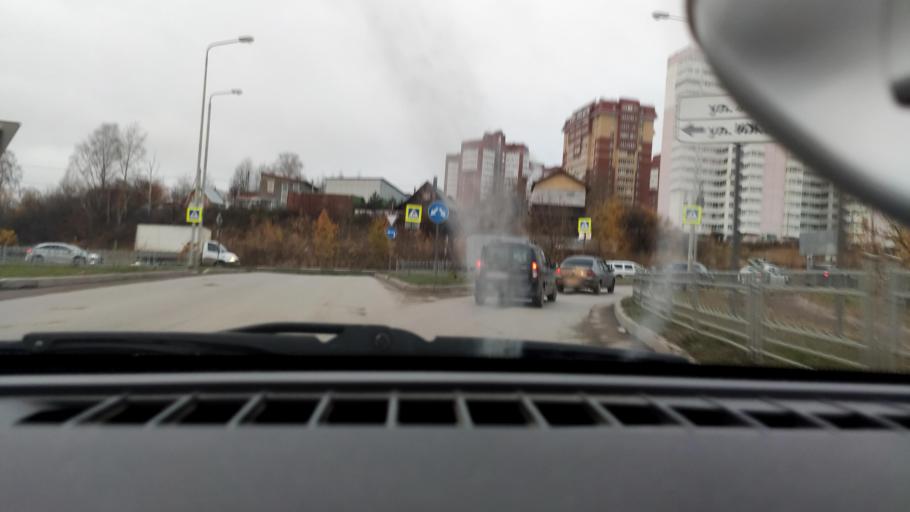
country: RU
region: Perm
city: Perm
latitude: 57.9825
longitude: 56.2805
